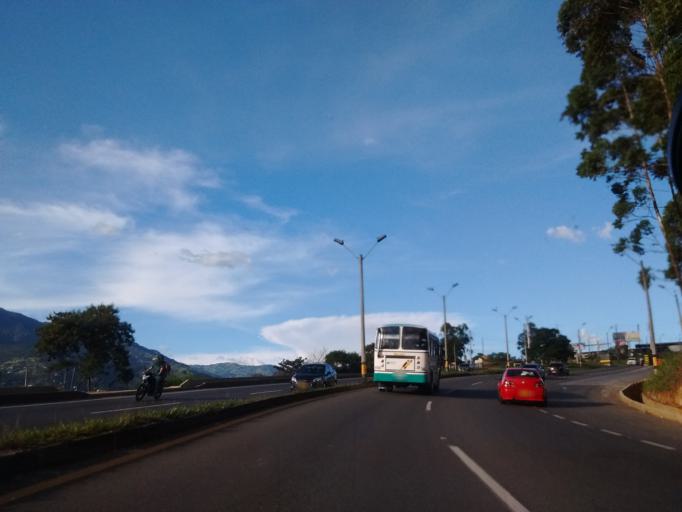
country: CO
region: Antioquia
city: Bello
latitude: 6.3224
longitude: -75.5445
